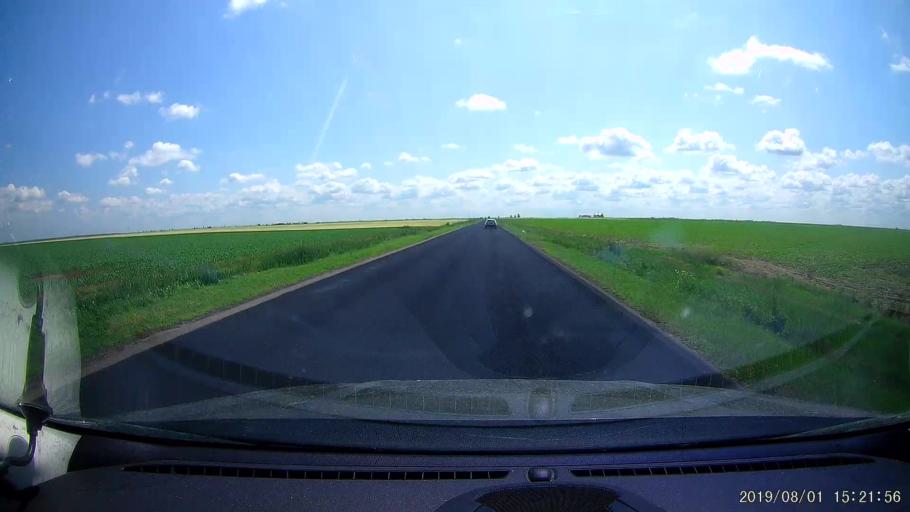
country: RO
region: Braila
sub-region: Comuna Tufesti
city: Tufesti
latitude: 45.0619
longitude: 27.7864
